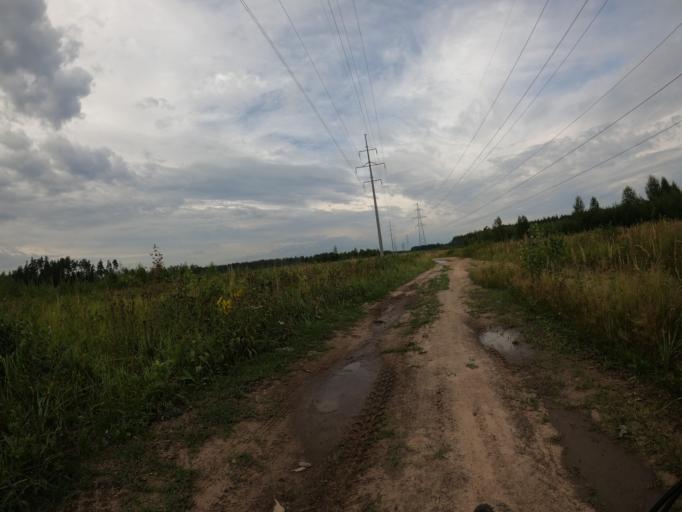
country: RU
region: Moskovskaya
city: Rodniki
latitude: 55.6703
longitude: 38.0800
